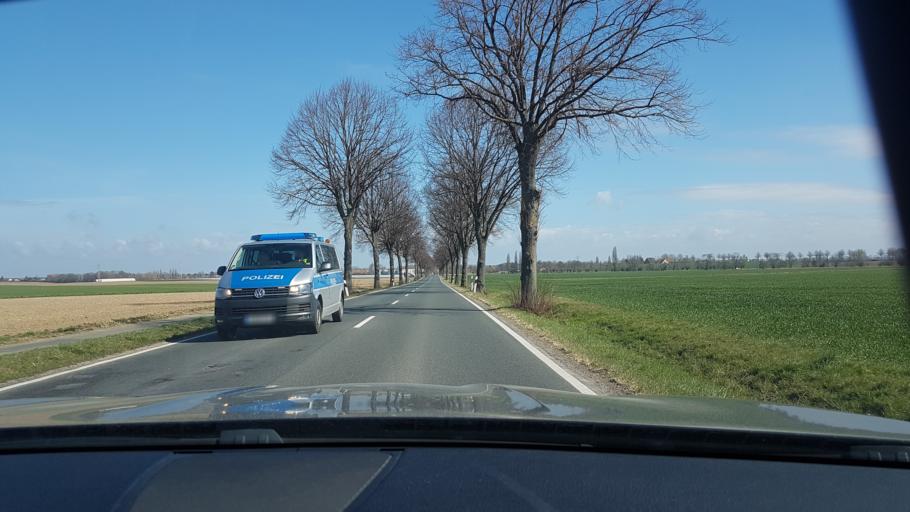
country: DE
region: Lower Saxony
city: Pattensen
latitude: 52.2467
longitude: 9.7403
